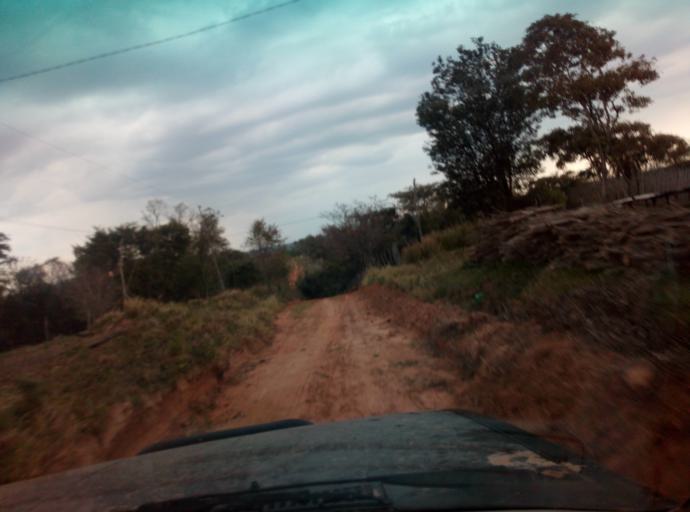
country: PY
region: Caaguazu
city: Doctor Cecilio Baez
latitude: -25.1434
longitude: -56.2242
